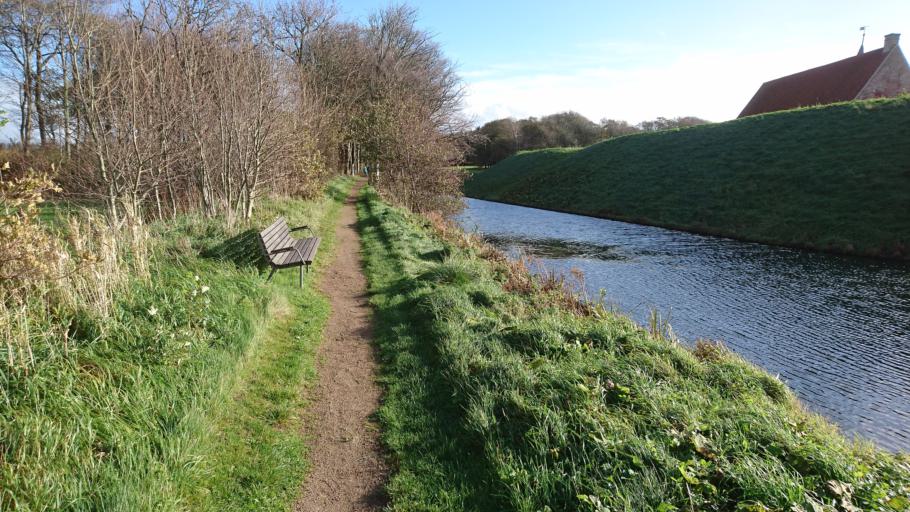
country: DK
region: Central Jutland
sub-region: Holstebro Kommune
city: Vinderup
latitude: 56.6404
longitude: 8.7818
